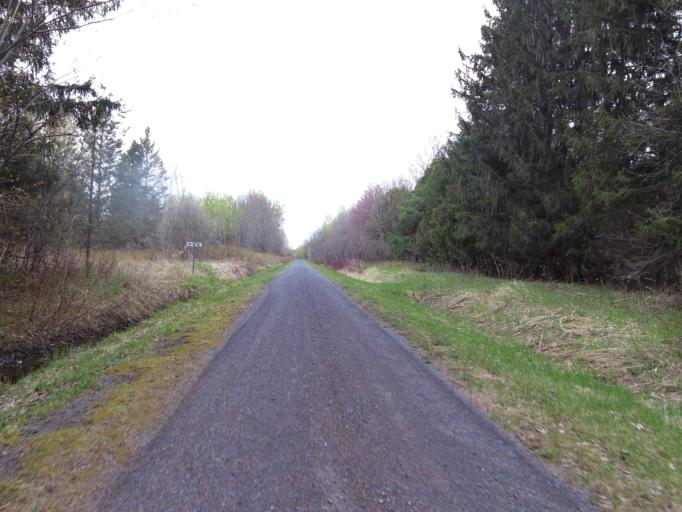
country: CA
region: Quebec
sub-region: Outaouais
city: Papineauville
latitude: 45.5191
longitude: -74.9625
